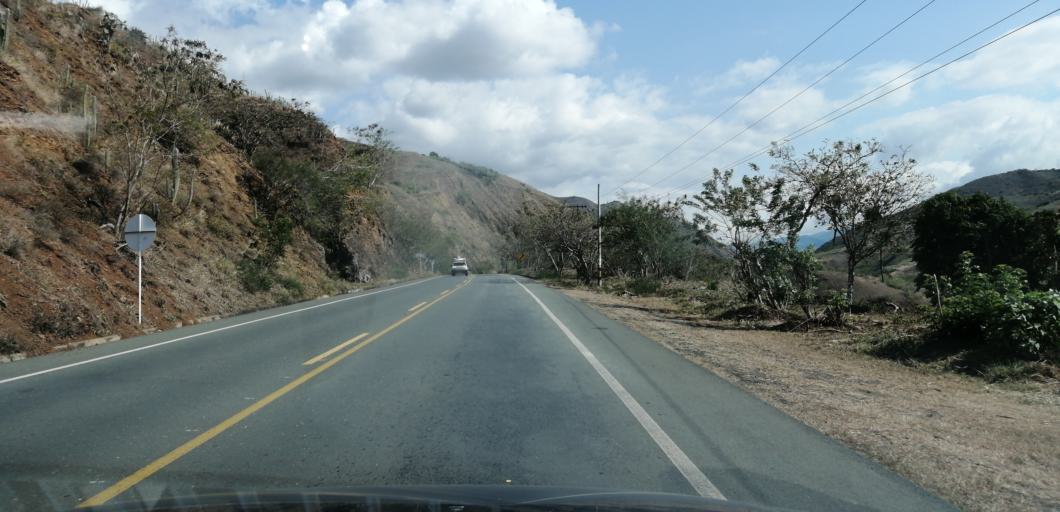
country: CO
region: Valle del Cauca
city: Dagua
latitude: 3.7512
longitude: -76.6615
